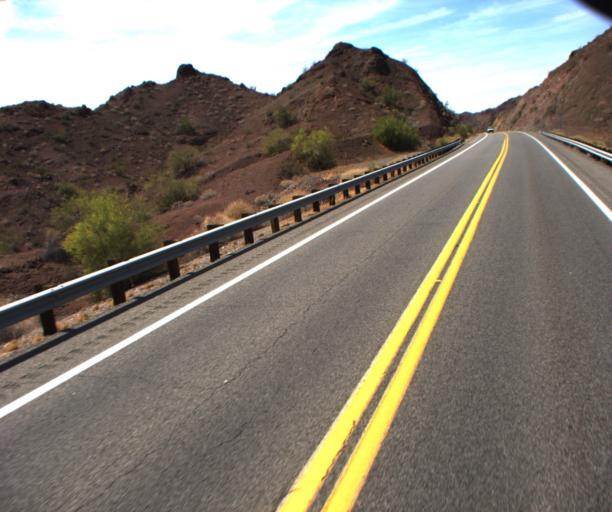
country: US
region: Arizona
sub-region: La Paz County
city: Cienega Springs
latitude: 34.3188
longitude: -114.1156
